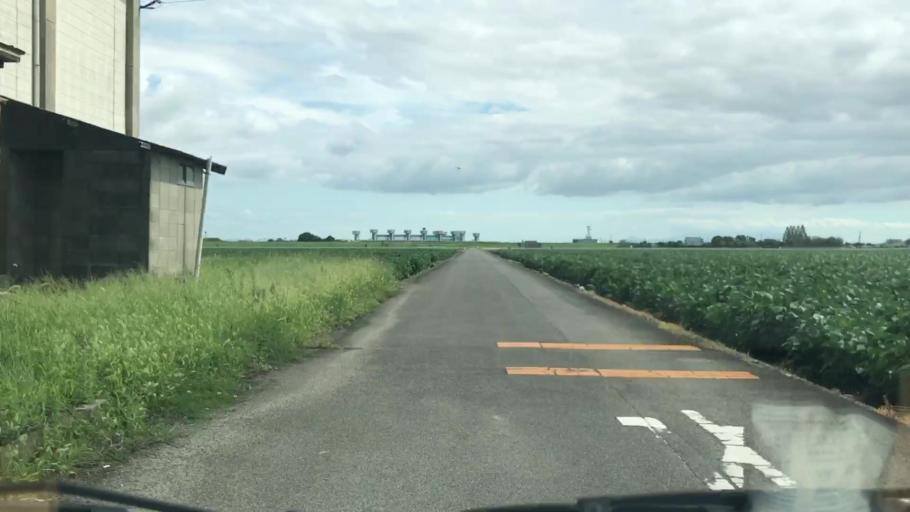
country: JP
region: Saga Prefecture
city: Saga-shi
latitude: 33.2136
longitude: 130.1832
